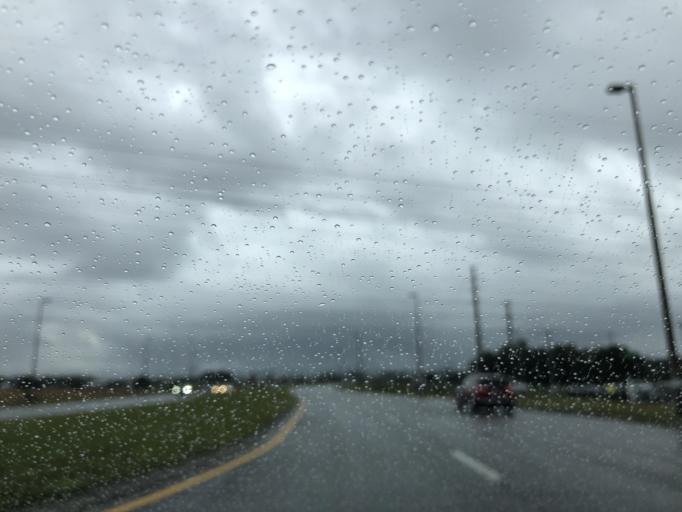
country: US
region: Florida
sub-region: Osceola County
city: Celebration
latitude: 28.3421
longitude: -81.5237
